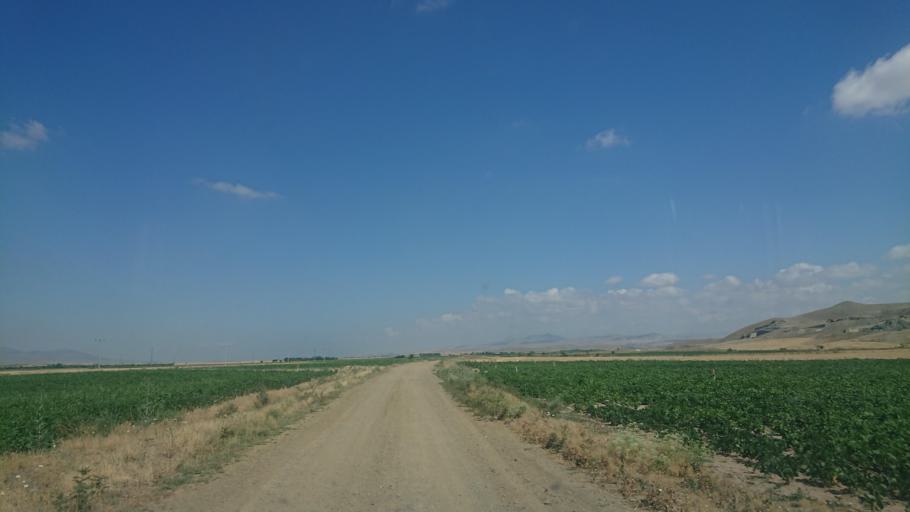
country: TR
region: Aksaray
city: Sariyahsi
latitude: 38.9746
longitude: 33.9145
